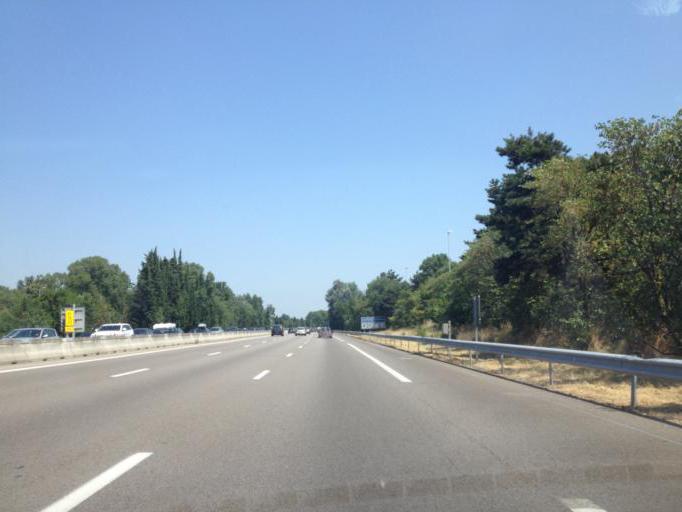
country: FR
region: Rhone-Alpes
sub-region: Departement de l'Ardeche
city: Guilherand-Granges
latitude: 44.9144
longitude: 4.8775
